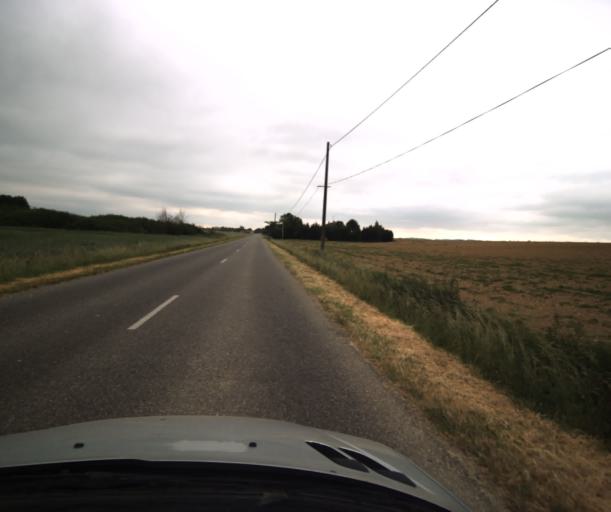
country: FR
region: Midi-Pyrenees
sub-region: Departement du Tarn-et-Garonne
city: Saint-Nicolas-de-la-Grave
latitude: 44.0340
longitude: 1.0189
